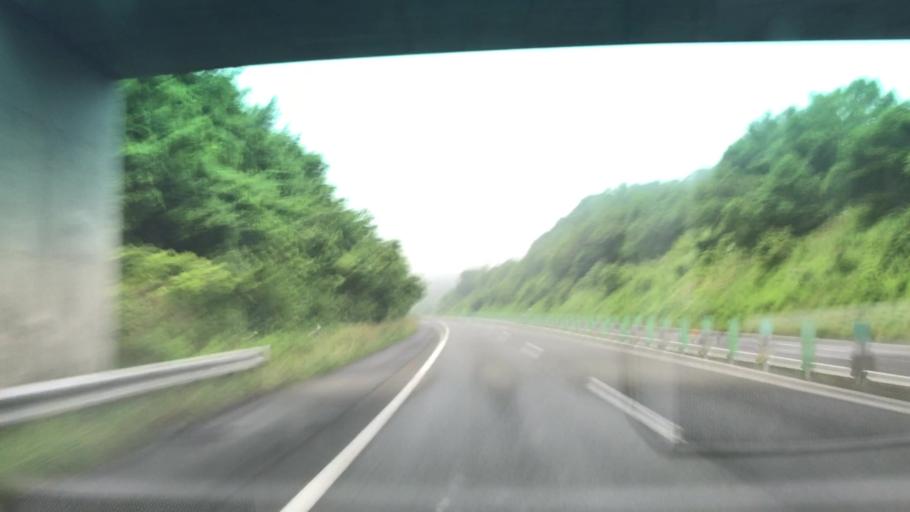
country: JP
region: Hokkaido
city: Shiraoi
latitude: 42.4819
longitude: 141.2224
